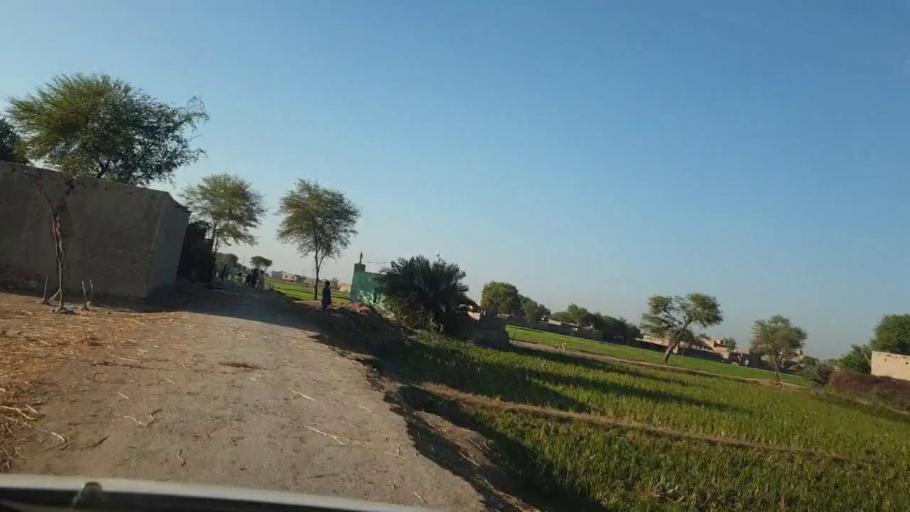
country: PK
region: Sindh
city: Khairpur Nathan Shah
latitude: 27.0423
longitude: 67.7284
